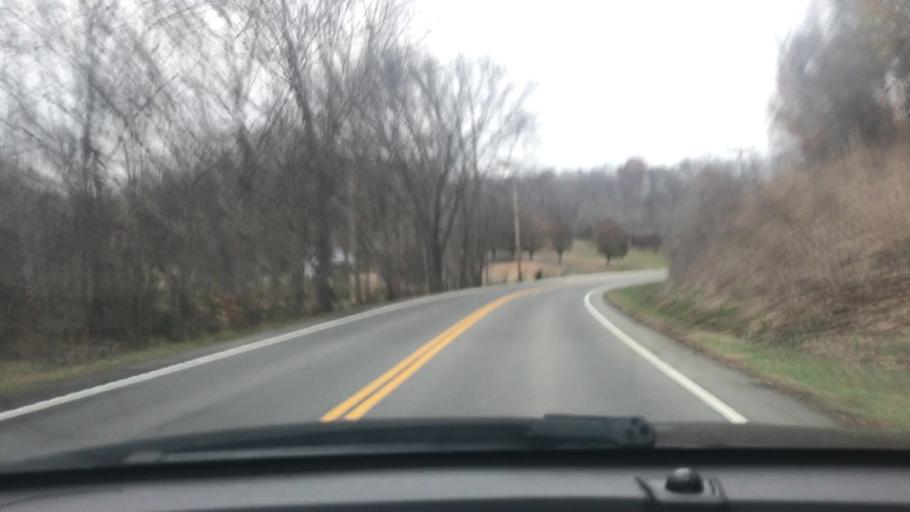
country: US
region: Tennessee
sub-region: Dickson County
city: Charlotte
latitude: 36.2430
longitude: -87.3473
